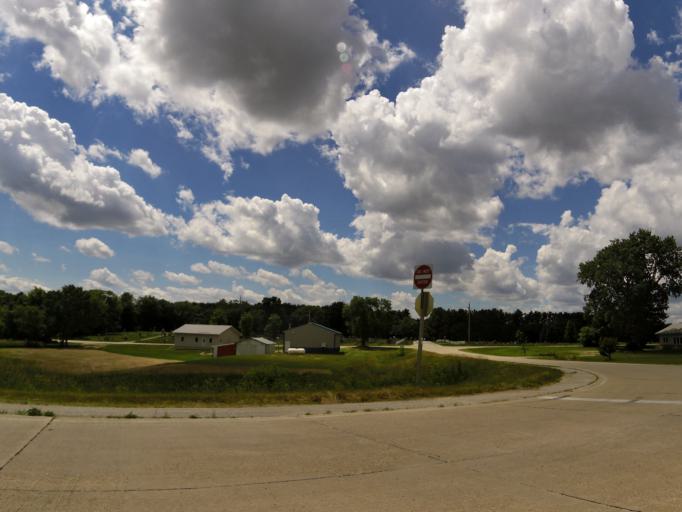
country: US
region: Iowa
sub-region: Fayette County
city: Oelwein
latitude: 42.6040
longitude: -91.9029
